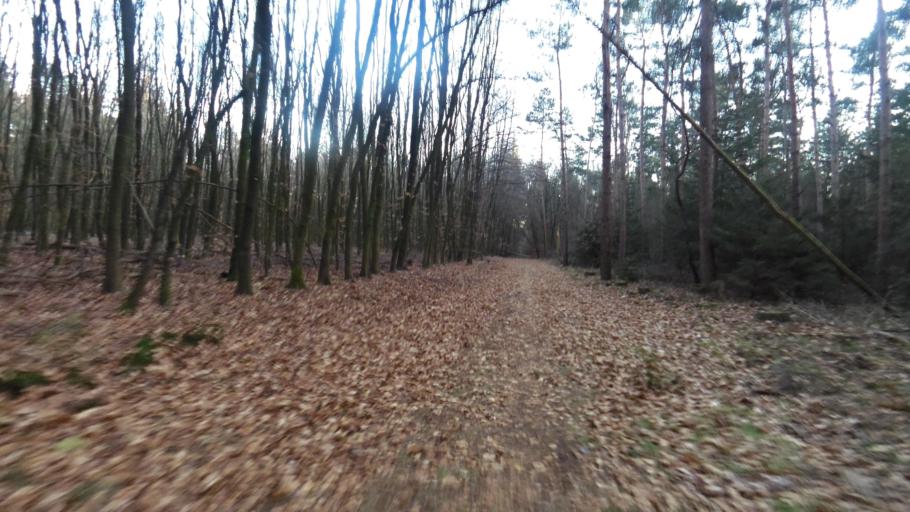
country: NL
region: Gelderland
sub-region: Gemeente Barneveld
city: Garderen
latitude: 52.2343
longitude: 5.6807
